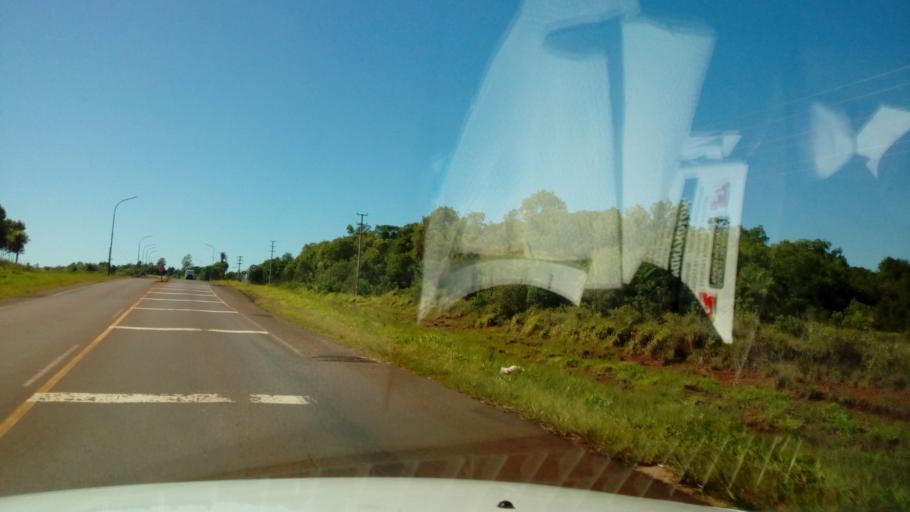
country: AR
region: Misiones
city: Santa Ana
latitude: -27.4023
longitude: -55.5569
